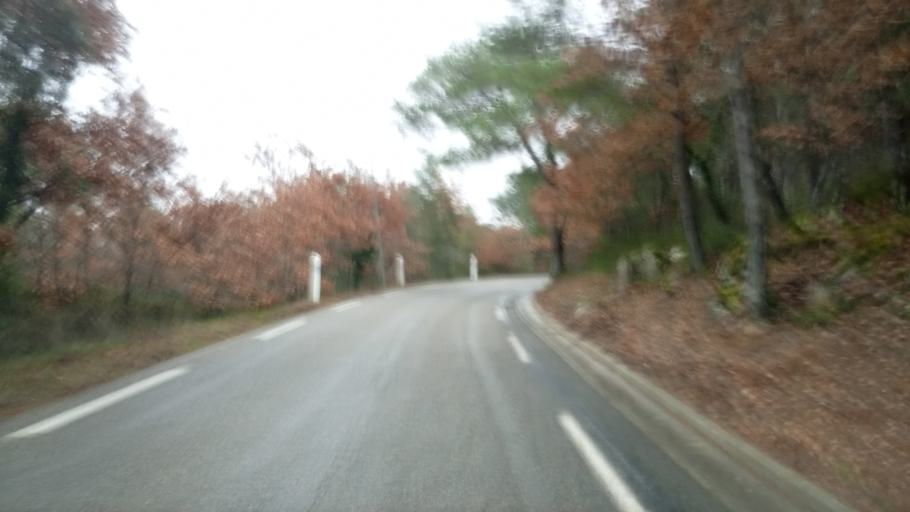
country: FR
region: Provence-Alpes-Cote d'Azur
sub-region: Departement du Var
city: Ginasservis
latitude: 43.7074
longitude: 5.8697
